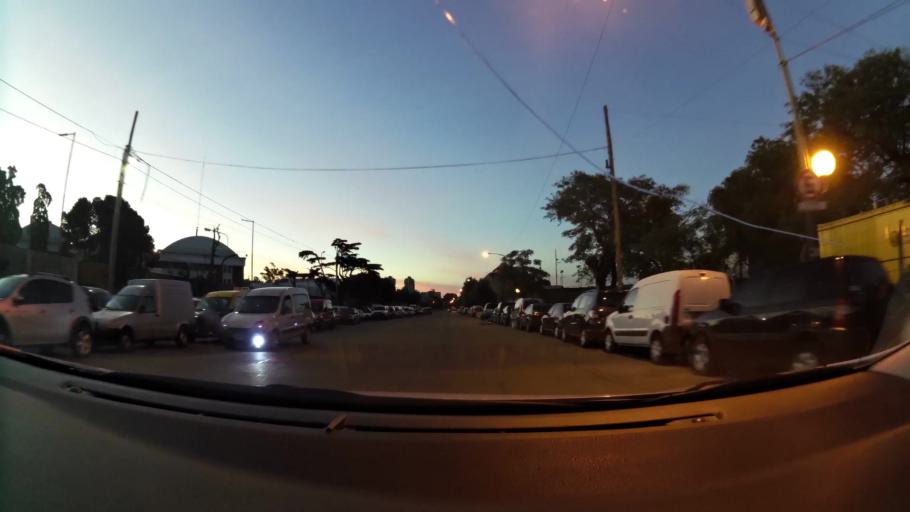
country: AR
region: Buenos Aires F.D.
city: Villa Lugano
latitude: -34.6490
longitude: -58.4470
